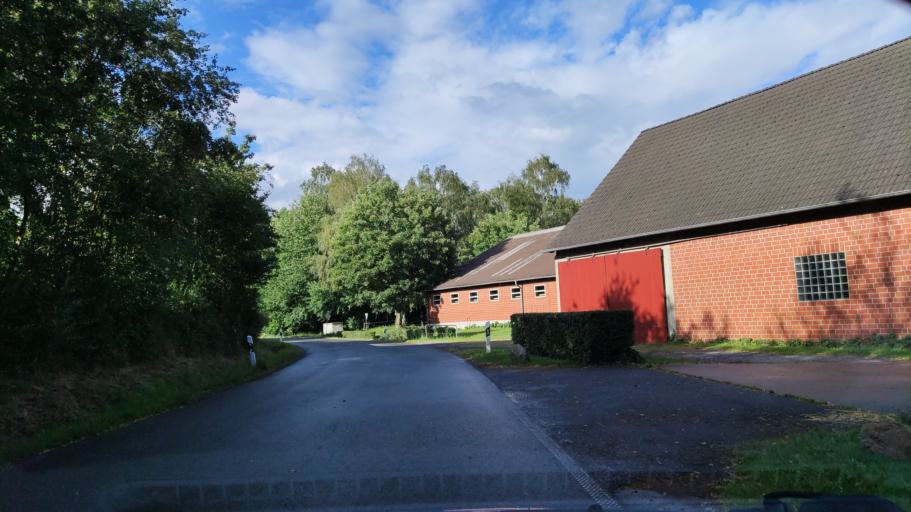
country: DE
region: North Rhine-Westphalia
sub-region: Regierungsbezirk Arnsberg
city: Welver
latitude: 51.6451
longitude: 7.9637
